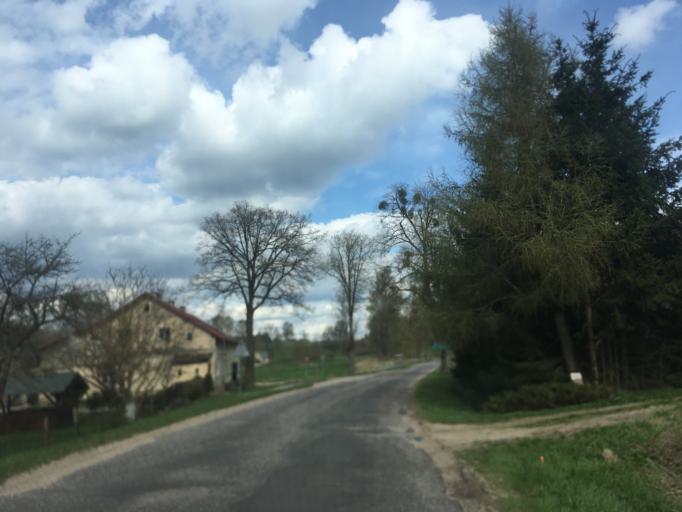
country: PL
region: Podlasie
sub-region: Powiat suwalski
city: Filipow
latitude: 54.2919
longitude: 22.6140
